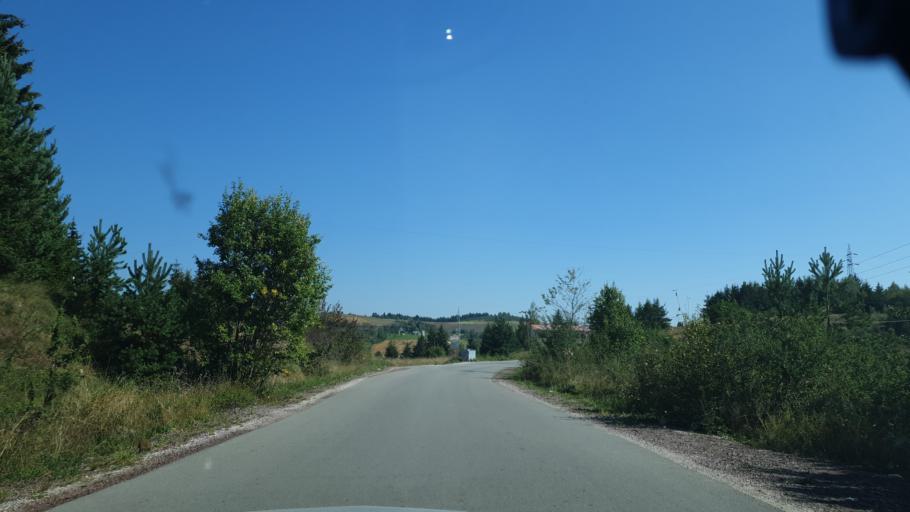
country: RS
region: Central Serbia
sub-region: Zlatiborski Okrug
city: Nova Varos
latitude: 43.4302
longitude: 19.8879
